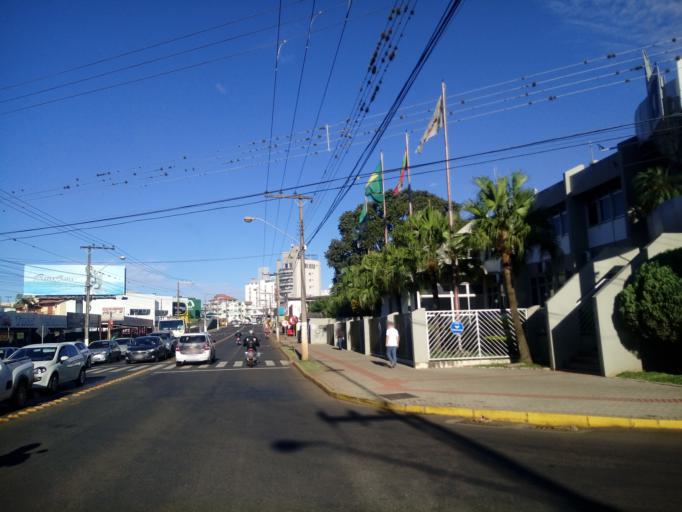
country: BR
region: Santa Catarina
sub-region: Chapeco
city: Chapeco
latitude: -27.0932
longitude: -52.6233
